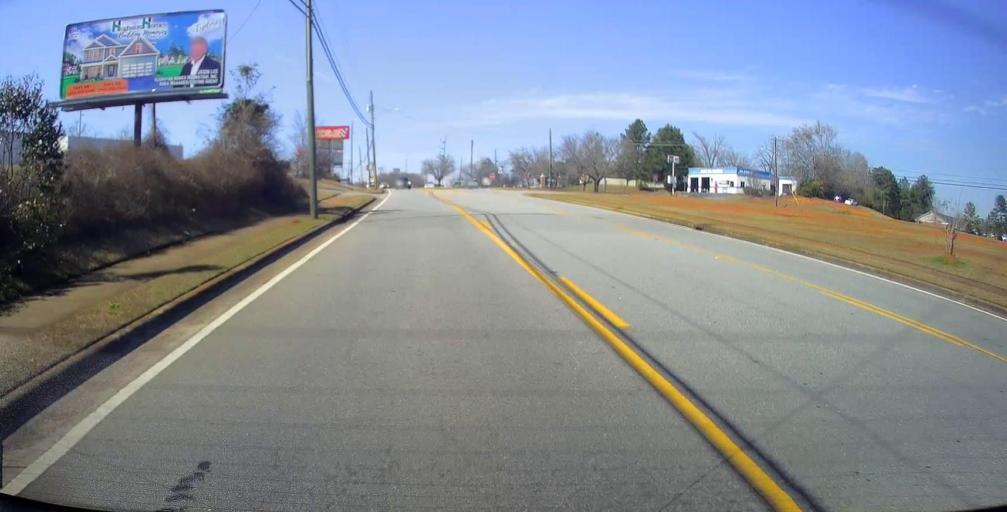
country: US
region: Georgia
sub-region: Houston County
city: Perry
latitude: 32.4646
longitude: -83.7371
